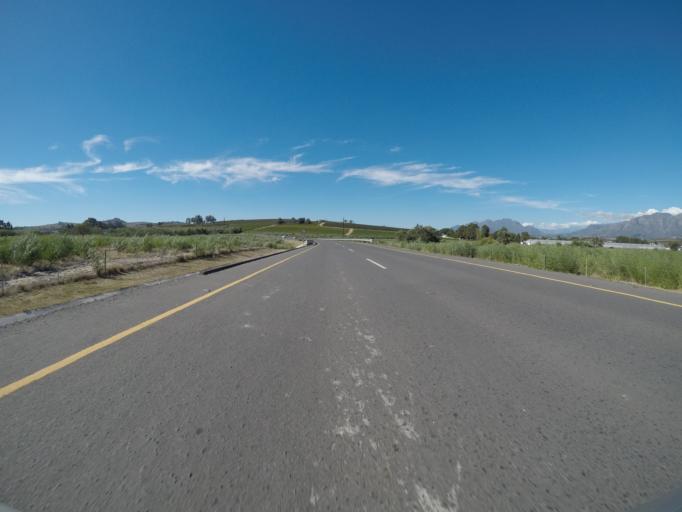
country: ZA
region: Western Cape
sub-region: Cape Winelands District Municipality
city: Stellenbosch
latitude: -33.9935
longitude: 18.7592
